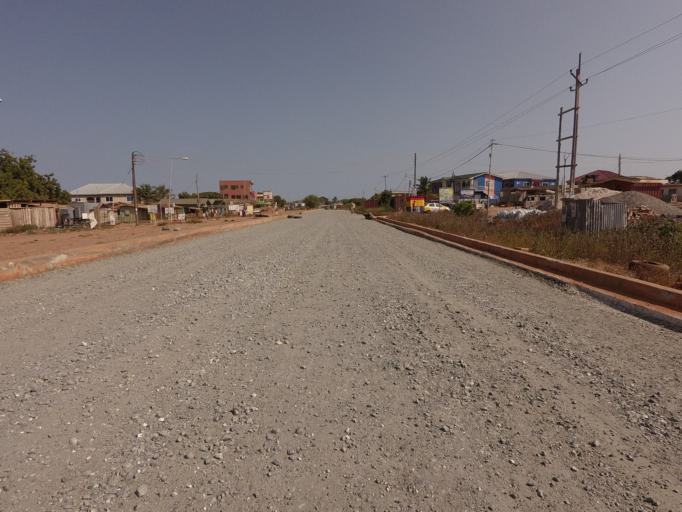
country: GH
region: Greater Accra
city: Teshi Old Town
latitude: 5.5920
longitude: -0.1162
